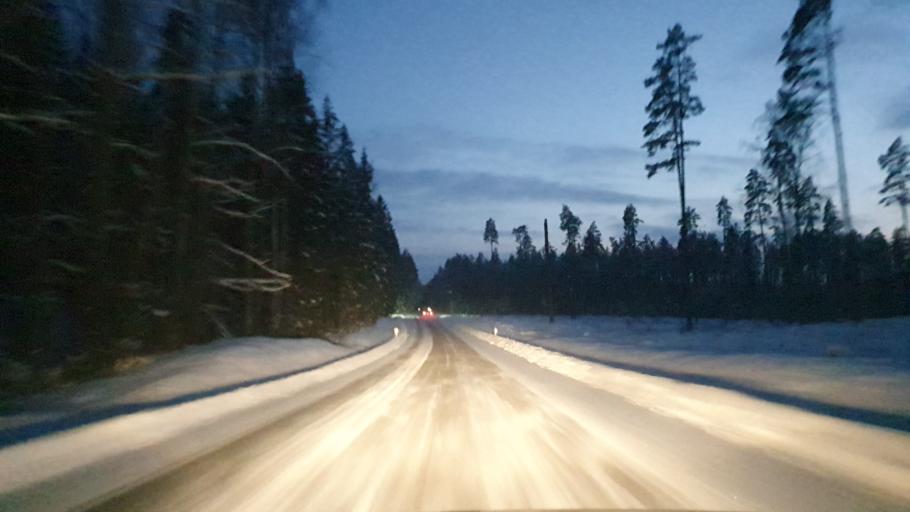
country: EE
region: Vorumaa
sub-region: Antsla vald
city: Vana-Antsla
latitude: 57.9731
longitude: 26.7597
